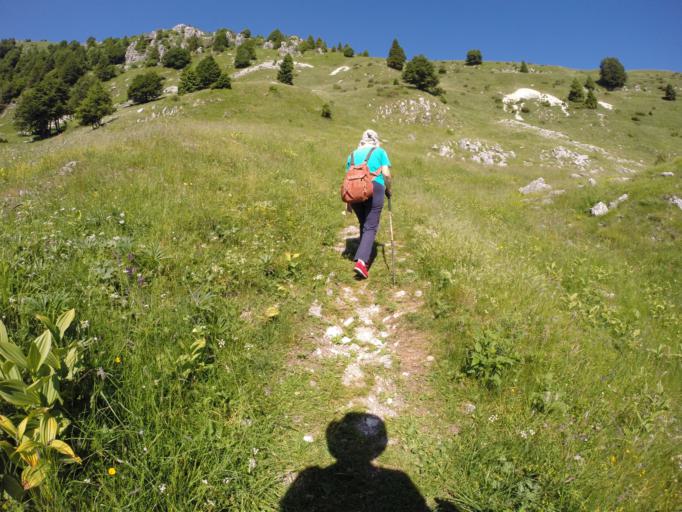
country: IT
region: Veneto
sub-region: Provincia di Treviso
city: Crespano del Grappa
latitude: 45.8838
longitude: 11.8066
